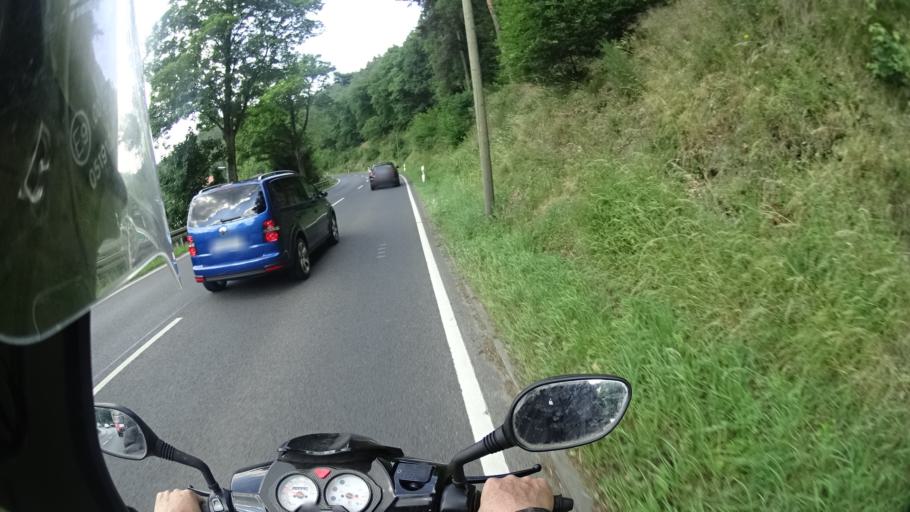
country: DE
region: Hesse
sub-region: Regierungsbezirk Darmstadt
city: Bad Schwalbach
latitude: 50.1465
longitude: 8.0863
